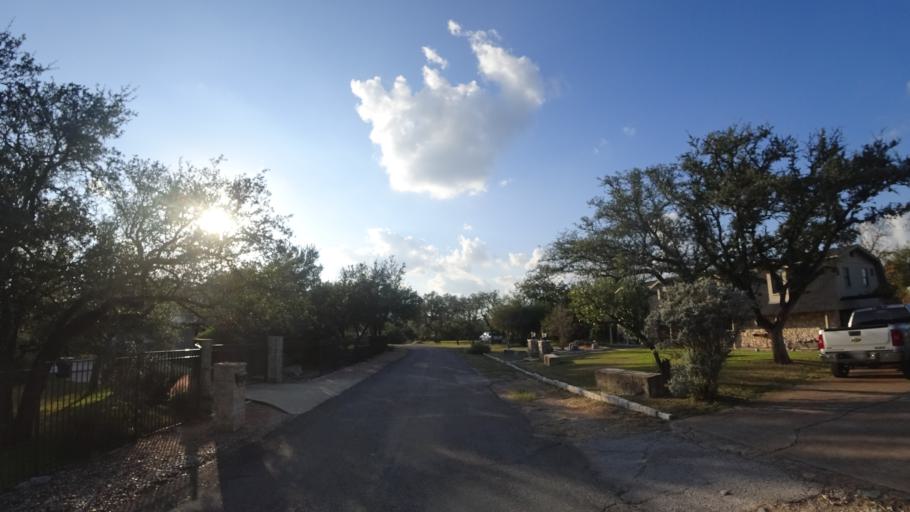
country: US
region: Texas
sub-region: Travis County
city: Lost Creek
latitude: 30.2955
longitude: -97.8473
